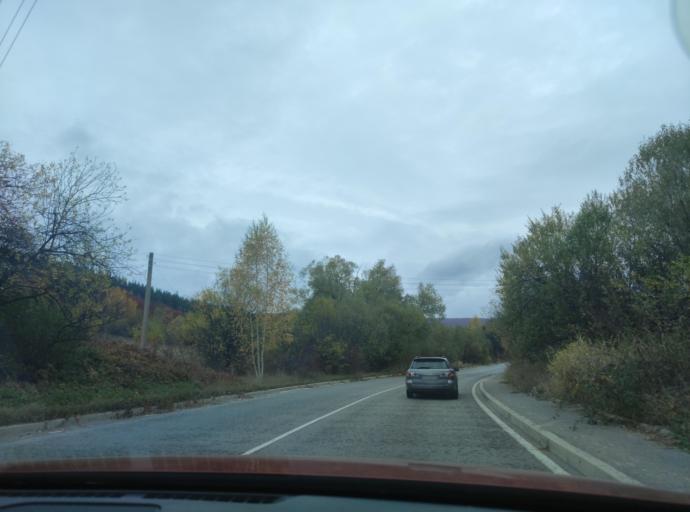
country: BG
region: Sofiya
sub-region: Obshtina Godech
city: Godech
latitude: 43.0908
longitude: 23.0980
